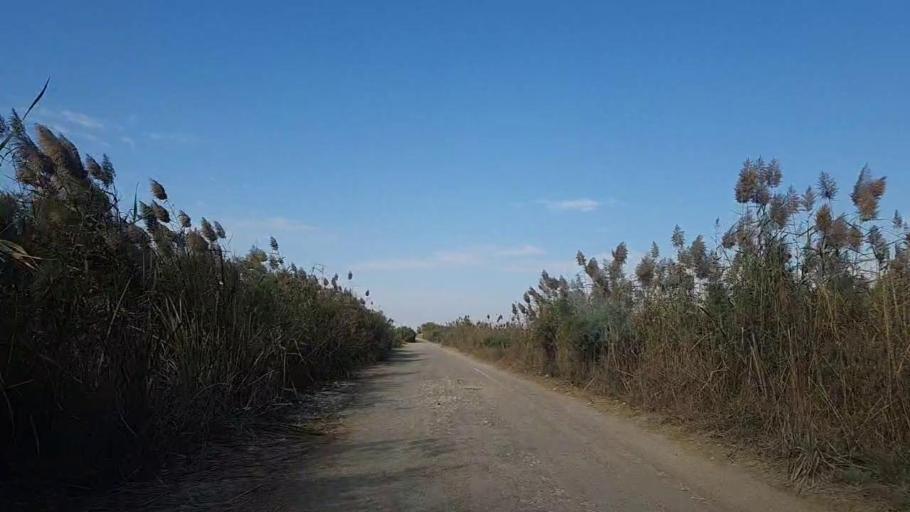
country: PK
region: Sindh
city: Khadro
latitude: 26.2964
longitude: 68.8202
